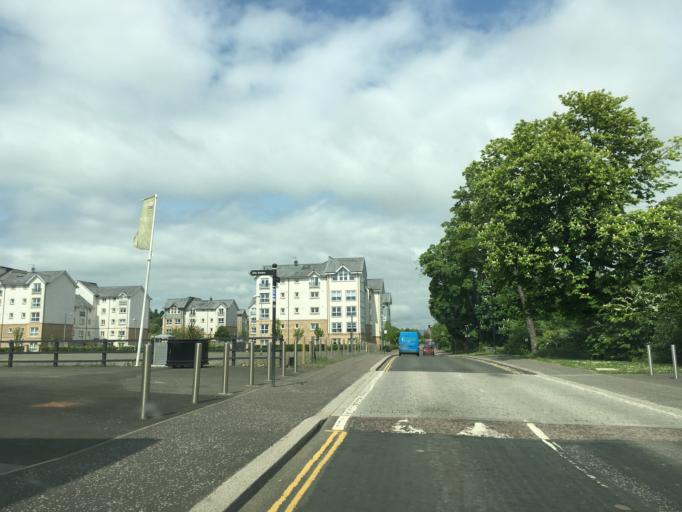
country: GB
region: Scotland
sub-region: Stirling
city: Stirling
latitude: 56.1196
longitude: -3.9319
